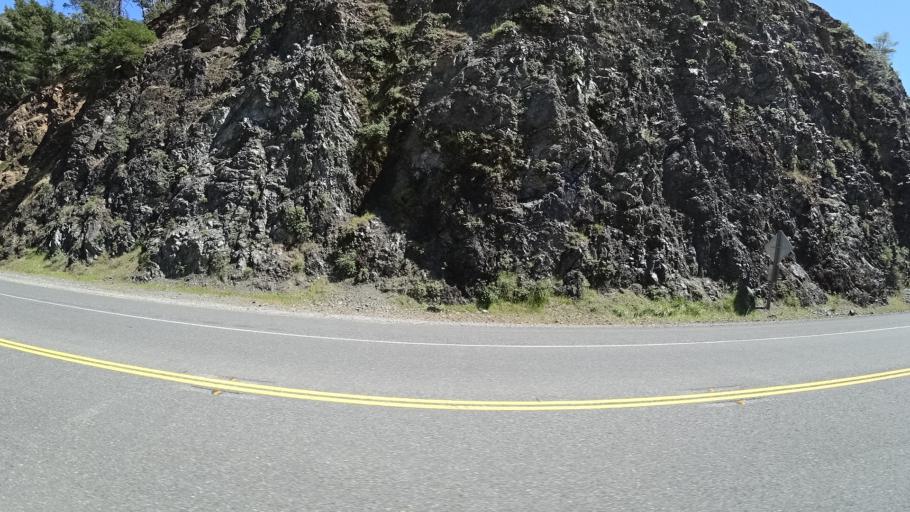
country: US
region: California
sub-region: Trinity County
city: Weaverville
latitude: 40.7411
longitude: -122.9988
